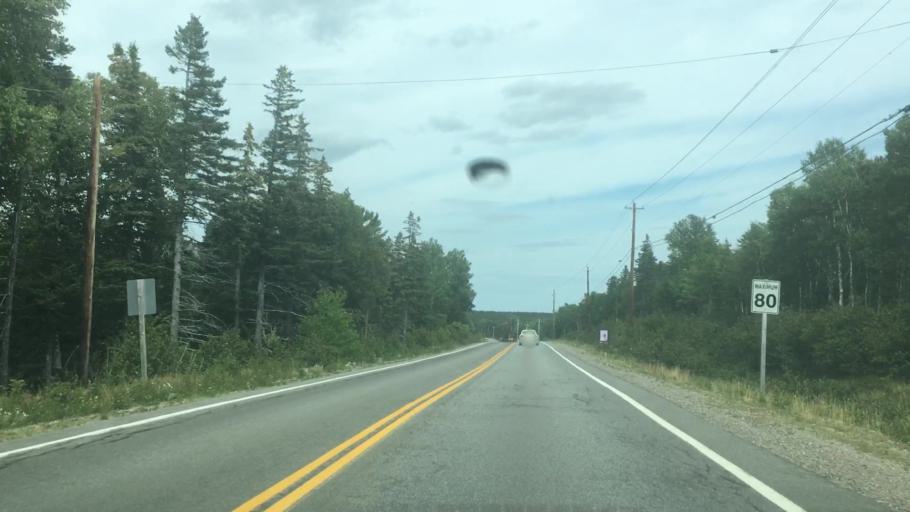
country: CA
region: Nova Scotia
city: Sydney Mines
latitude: 46.5038
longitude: -60.4357
